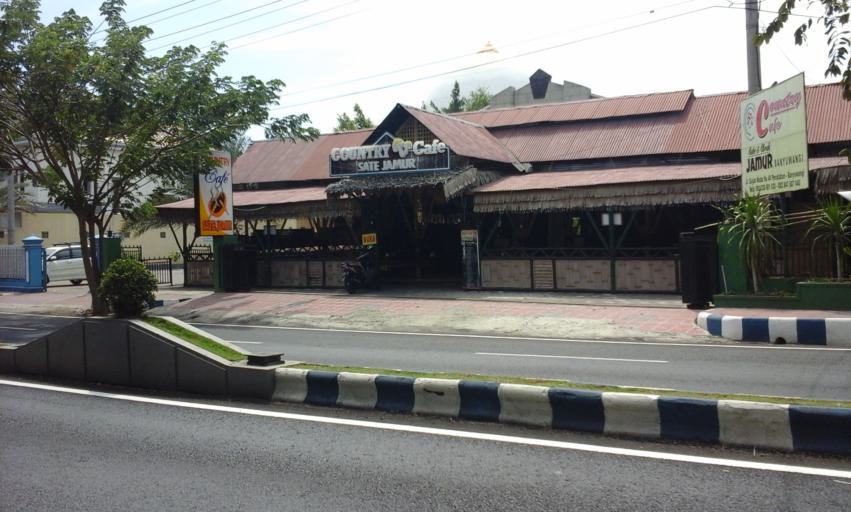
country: ID
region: East Java
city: Krajan Satu
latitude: -8.2103
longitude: 114.3563
